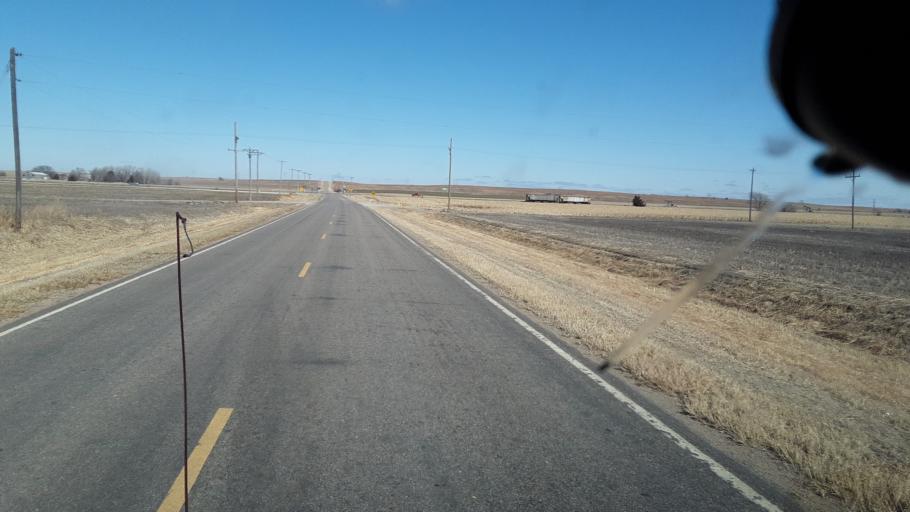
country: US
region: Kansas
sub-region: Barton County
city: Ellinwood
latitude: 38.3608
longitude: -98.6639
